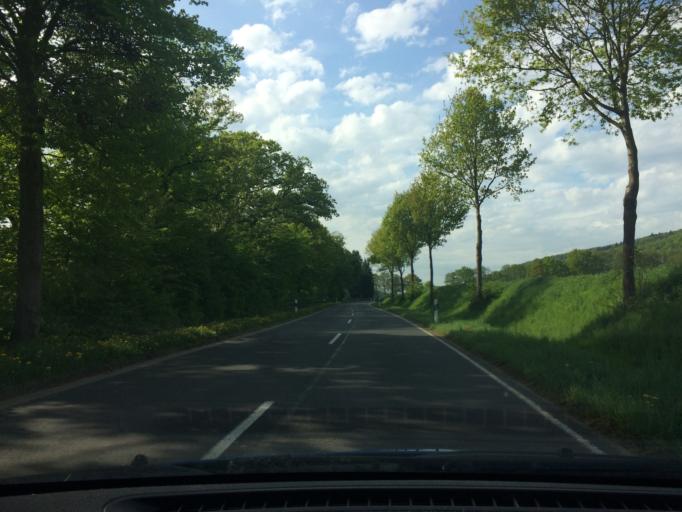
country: DE
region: Lower Saxony
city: Buhren
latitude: 51.5438
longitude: 9.6224
